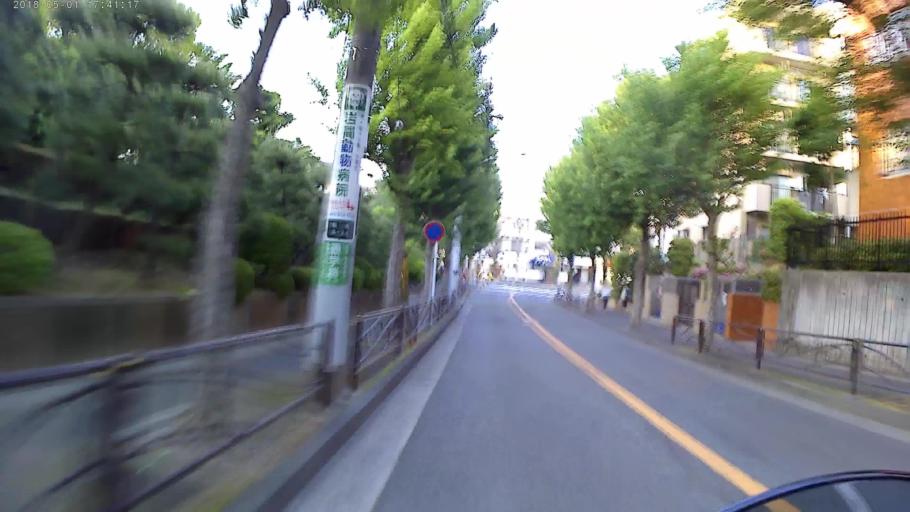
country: JP
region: Tokyo
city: Chofugaoka
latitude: 35.5728
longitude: 139.5769
